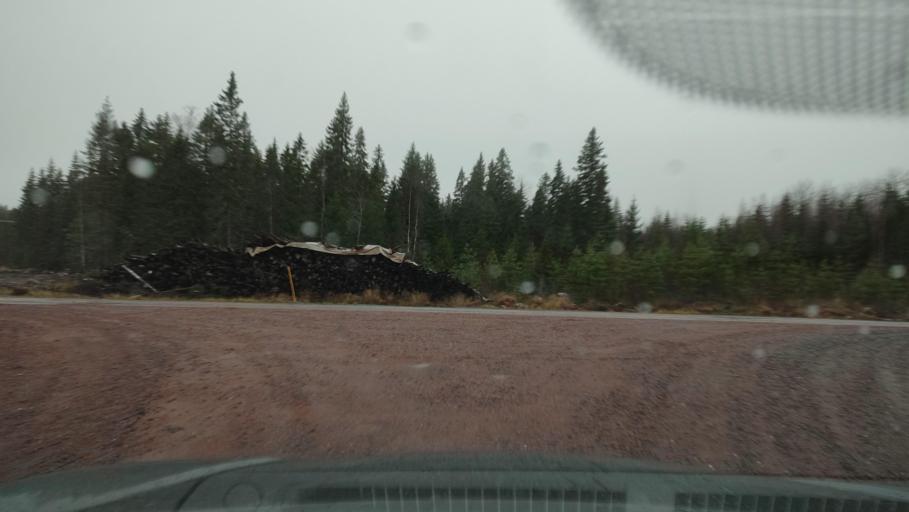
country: FI
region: Southern Ostrobothnia
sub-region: Suupohja
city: Karijoki
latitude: 62.1733
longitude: 21.7030
